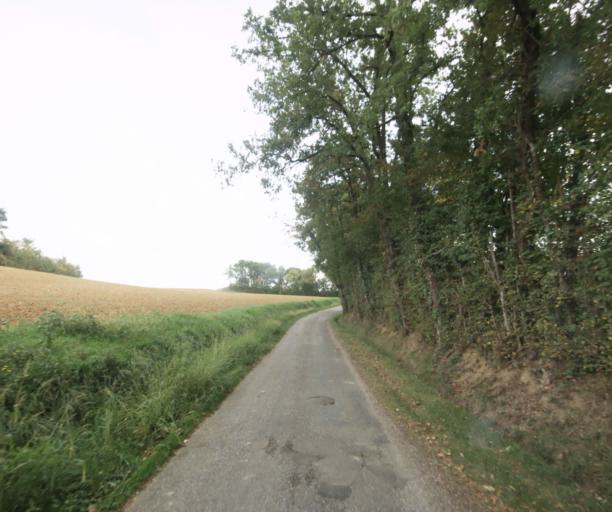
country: FR
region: Midi-Pyrenees
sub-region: Departement du Gers
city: Gondrin
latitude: 43.8640
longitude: 0.2610
